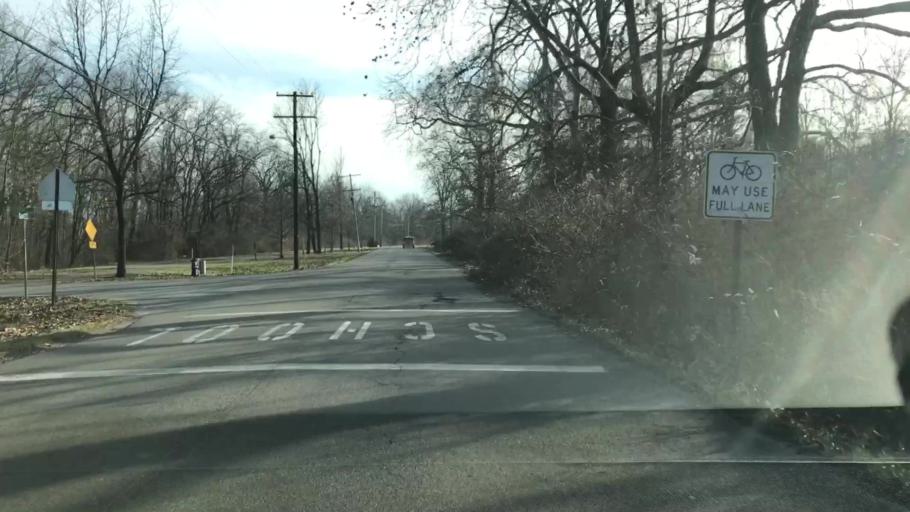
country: US
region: Ohio
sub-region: Greene County
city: Yellow Springs
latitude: 39.7947
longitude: -83.8838
